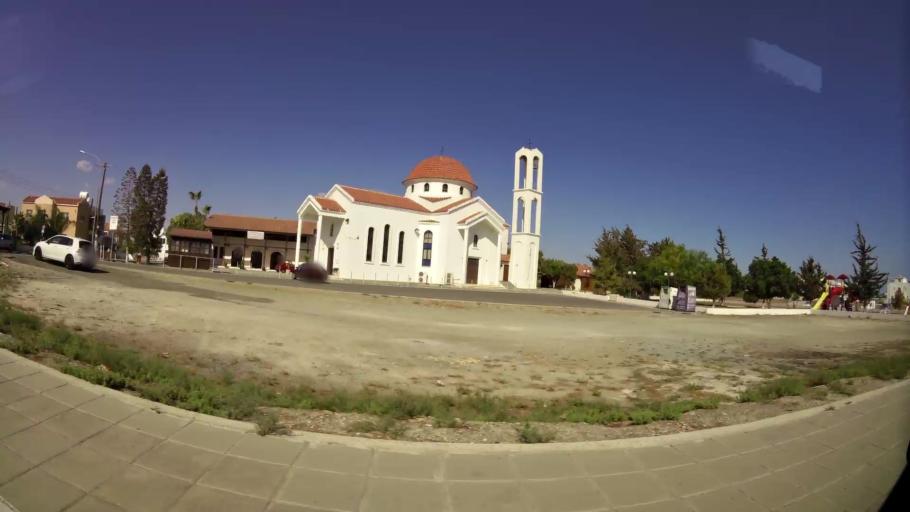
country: CY
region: Larnaka
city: Livadia
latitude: 34.9479
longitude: 33.6348
